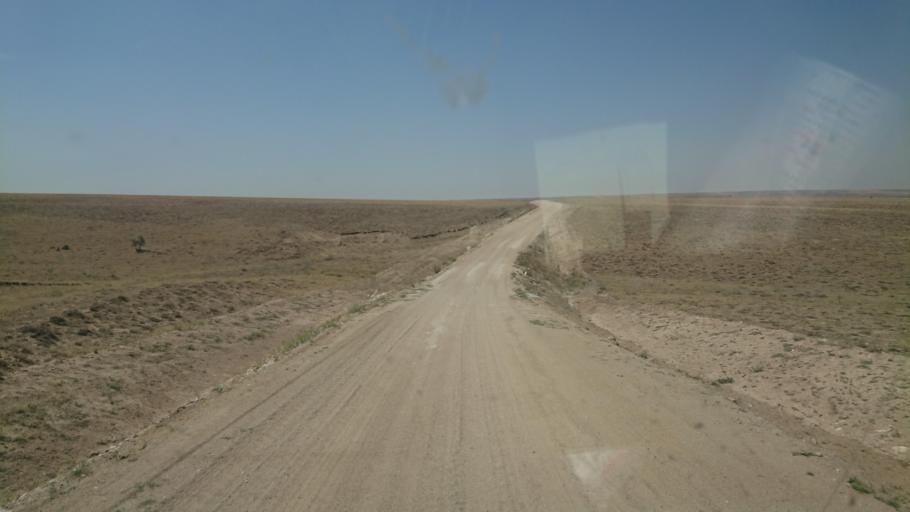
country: TR
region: Aksaray
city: Agacoren
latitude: 38.7414
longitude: 33.8859
